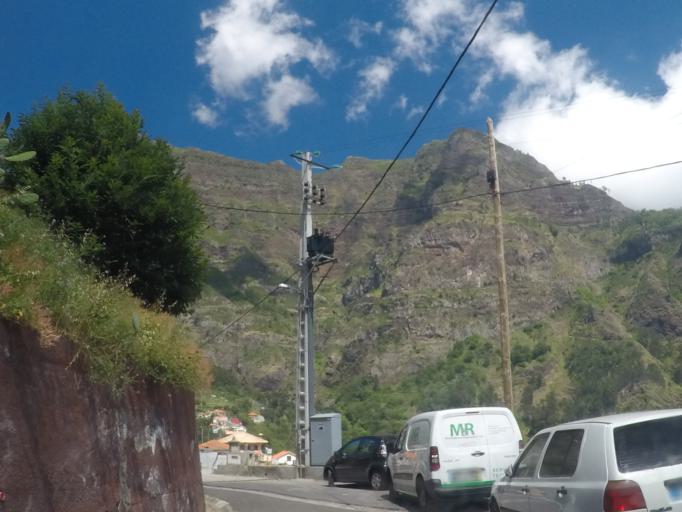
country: PT
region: Madeira
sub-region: Camara de Lobos
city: Curral das Freiras
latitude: 32.7179
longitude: -16.9734
